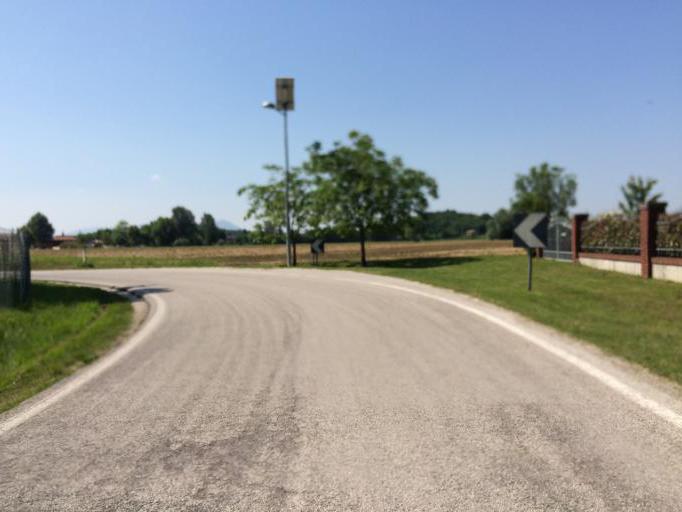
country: IT
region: Veneto
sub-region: Provincia di Vicenza
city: Montegalda
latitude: 45.4687
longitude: 11.6730
